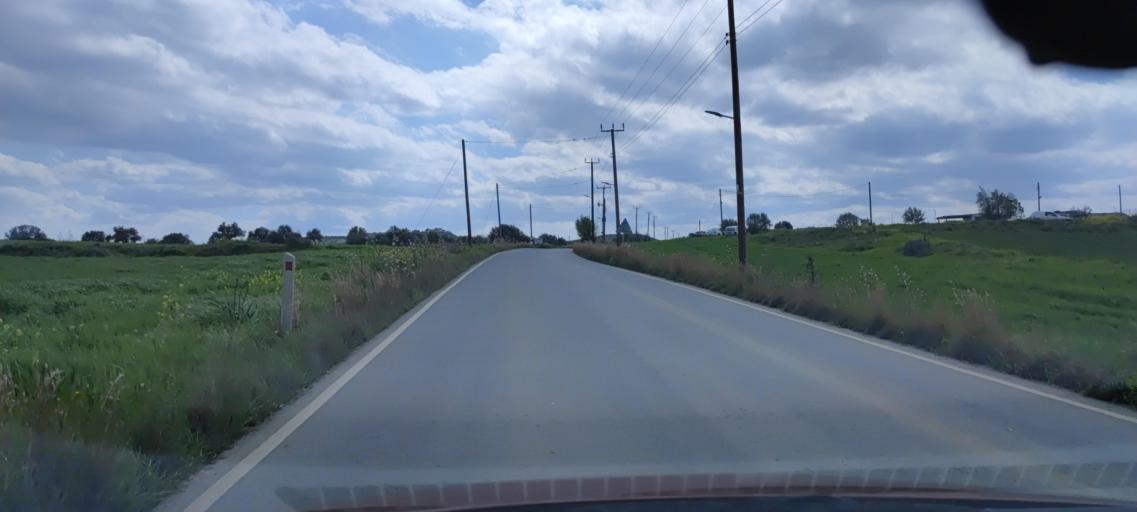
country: CY
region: Lefkosia
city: Tseri
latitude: 35.0465
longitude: 33.3183
